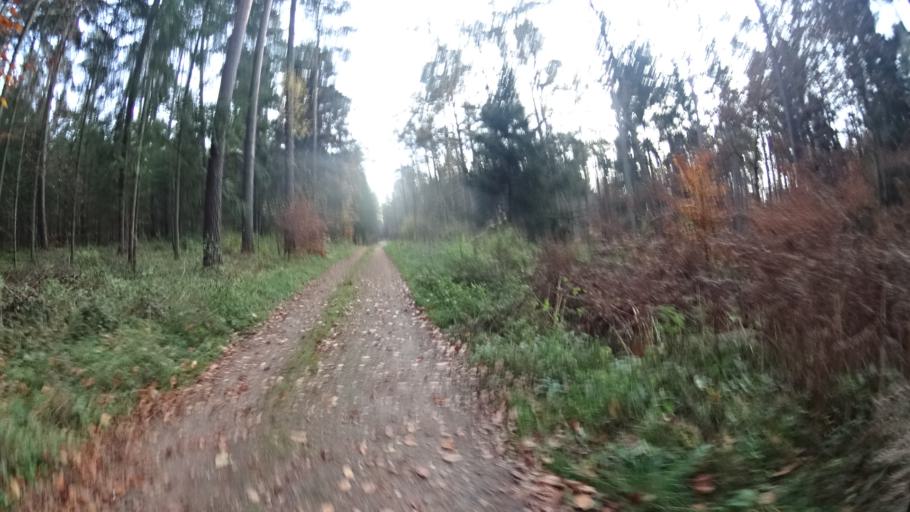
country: DE
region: Lower Saxony
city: Deutsch Evern
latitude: 53.2238
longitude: 10.4308
